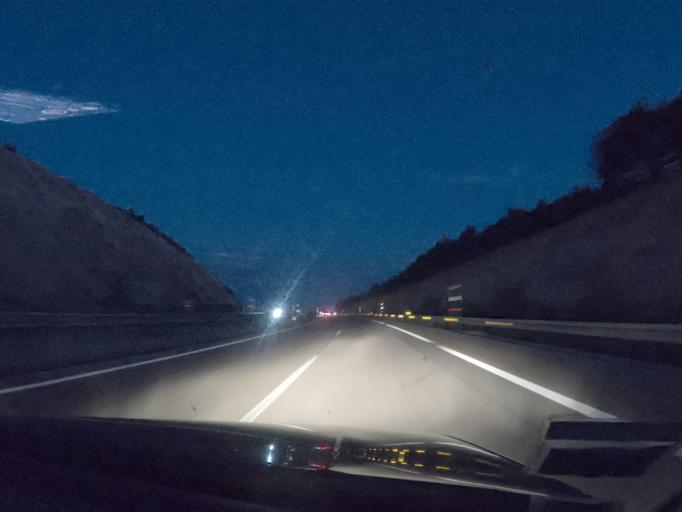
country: ES
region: Castille and Leon
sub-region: Provincia de Leon
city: Villagaton
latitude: 42.5660
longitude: -6.2126
